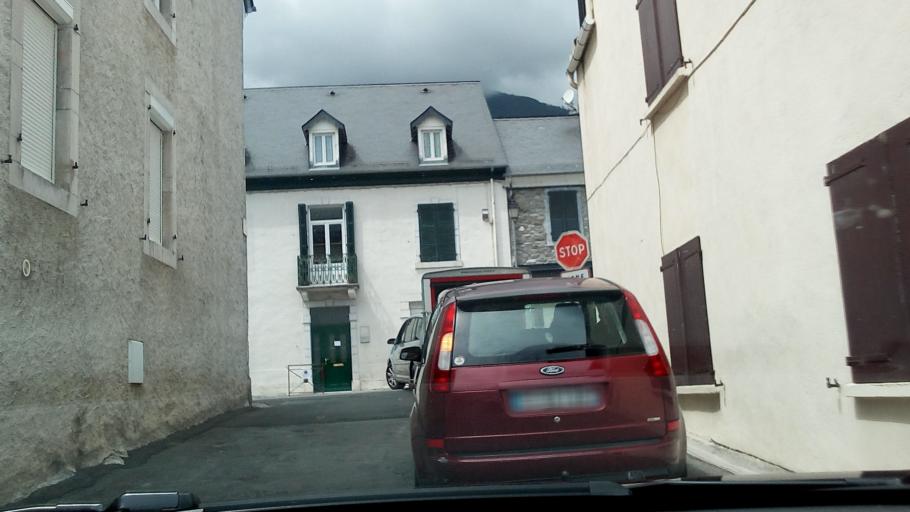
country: FR
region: Aquitaine
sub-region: Departement des Pyrenees-Atlantiques
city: Laruns
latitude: 42.9858
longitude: -0.4268
